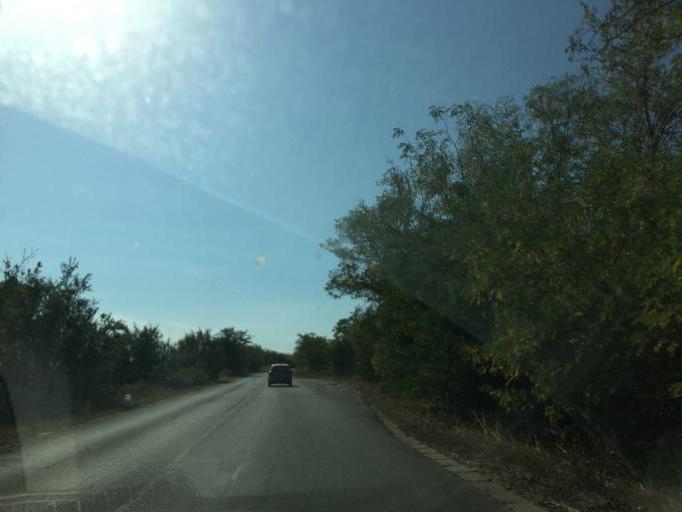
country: BG
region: Pazardzhik
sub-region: Obshtina Peshtera
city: Peshtera
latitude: 42.1074
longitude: 24.2975
